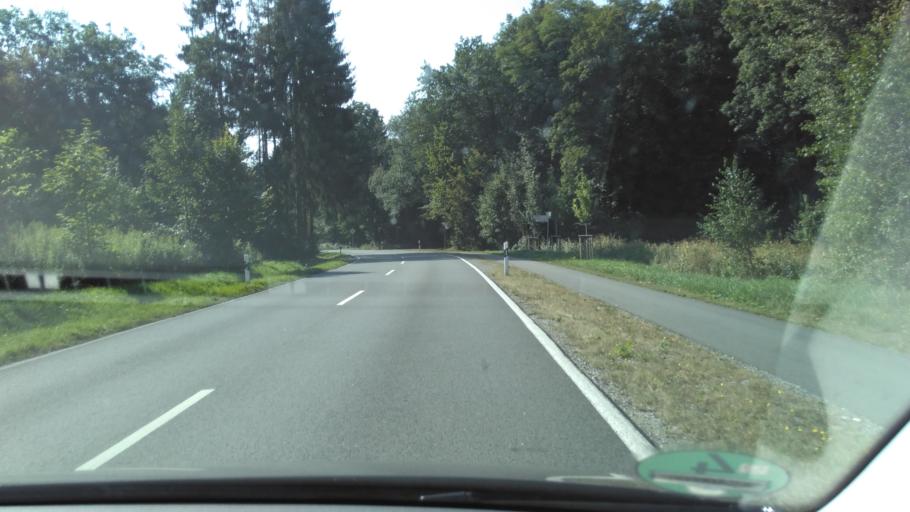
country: DE
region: North Rhine-Westphalia
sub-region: Regierungsbezirk Detmold
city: Oerlinghausen
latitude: 51.8992
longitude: 8.6048
